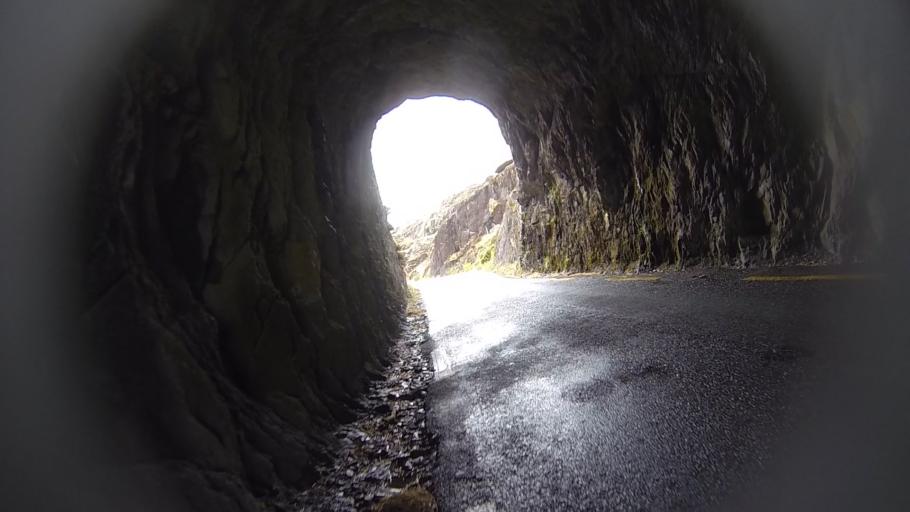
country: IE
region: Munster
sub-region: Ciarrai
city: Kenmare
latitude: 51.7922
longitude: -9.5919
